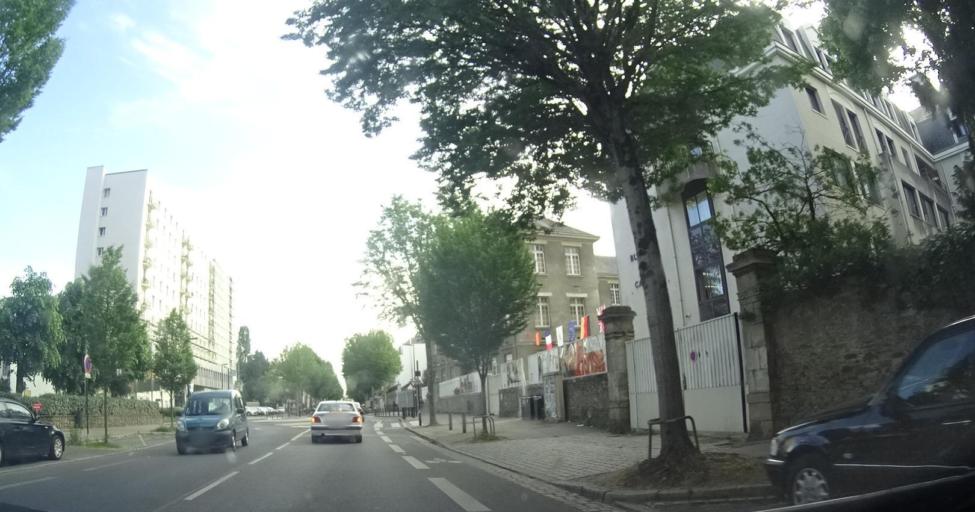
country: FR
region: Pays de la Loire
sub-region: Departement de la Loire-Atlantique
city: Nantes
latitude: 47.2375
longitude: -1.5330
